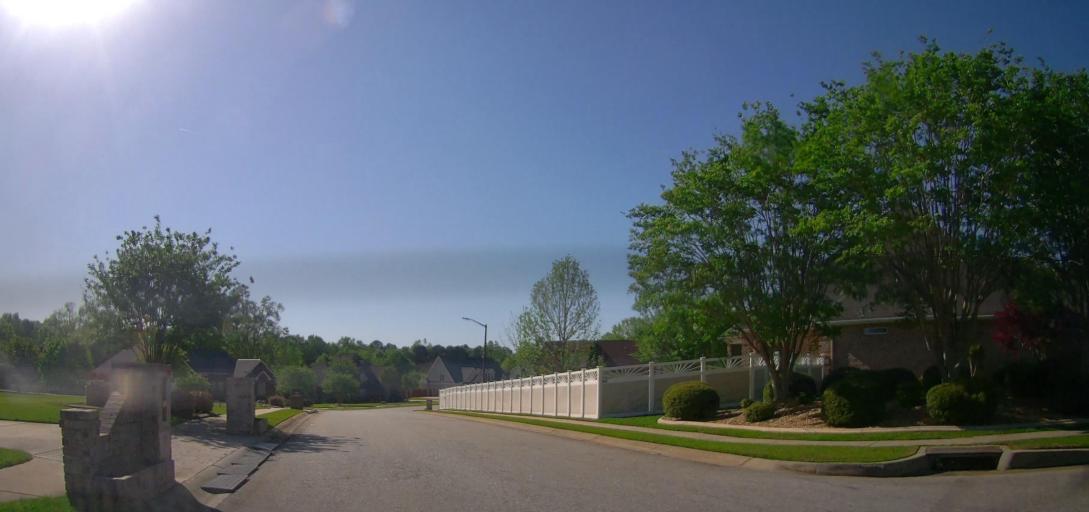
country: US
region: Georgia
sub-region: Houston County
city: Robins Air Force Base
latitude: 32.5418
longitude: -83.5902
